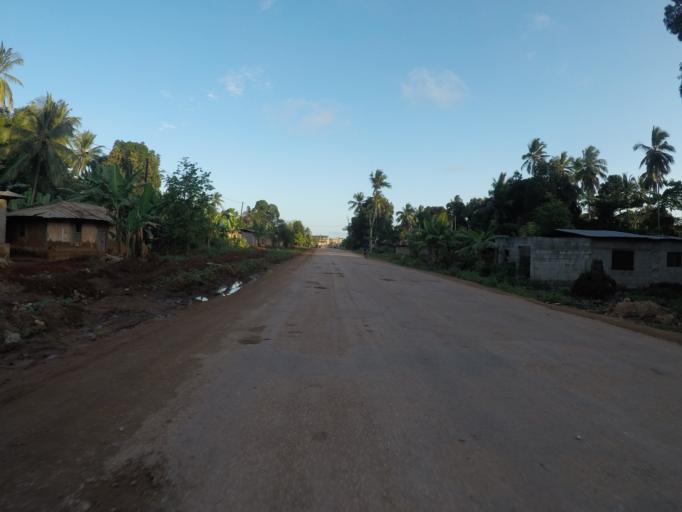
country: TZ
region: Zanzibar North
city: Gamba
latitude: -5.9041
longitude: 39.2968
